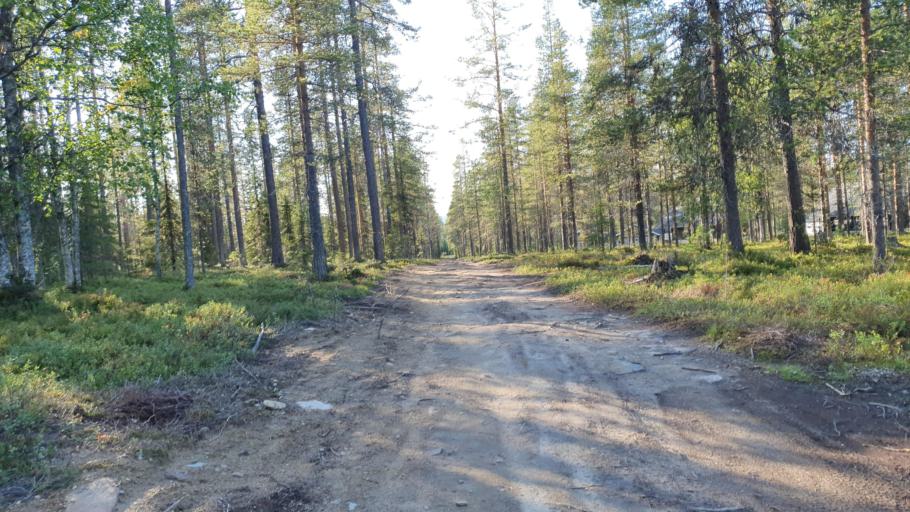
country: FI
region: Lapland
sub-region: Tunturi-Lappi
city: Kolari
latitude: 67.5996
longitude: 24.1906
